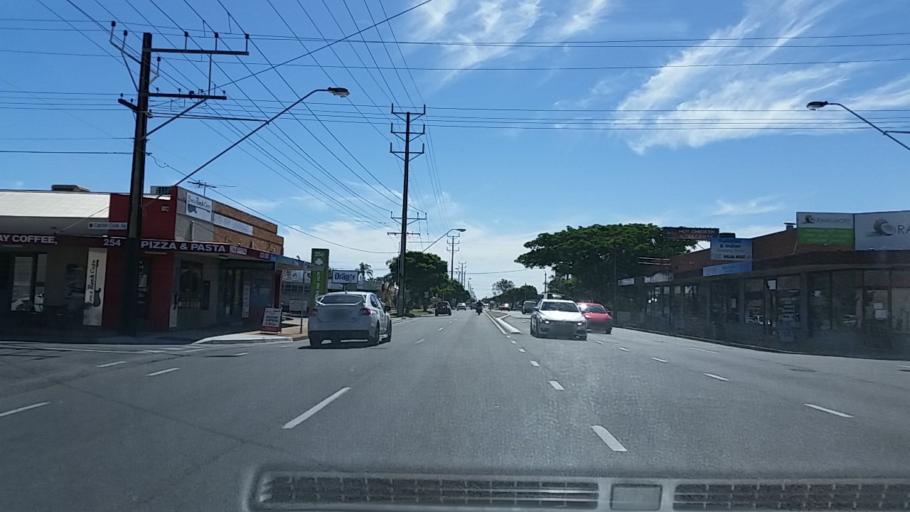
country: AU
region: South Australia
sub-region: Charles Sturt
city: Findon
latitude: -34.9052
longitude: 138.5390
